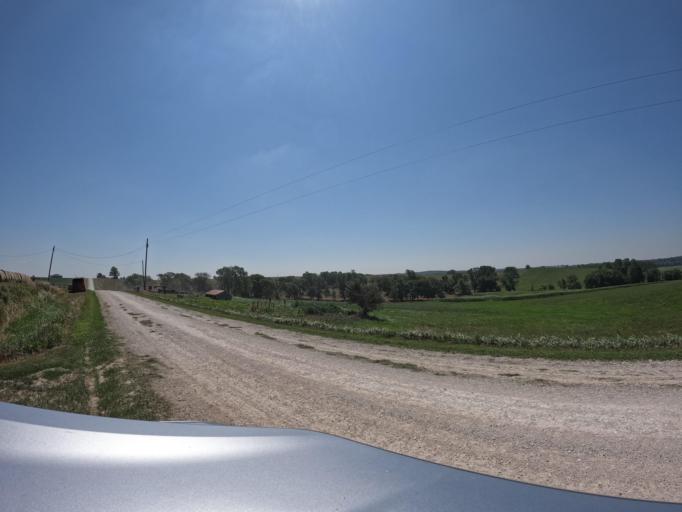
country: US
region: Iowa
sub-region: Keokuk County
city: Sigourney
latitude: 41.2500
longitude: -92.2147
